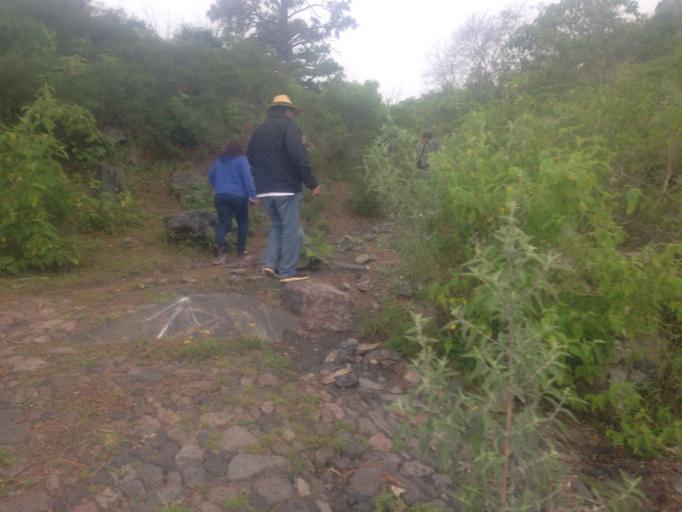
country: MX
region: Nayarit
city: Jala
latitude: 21.1340
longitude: -104.5021
